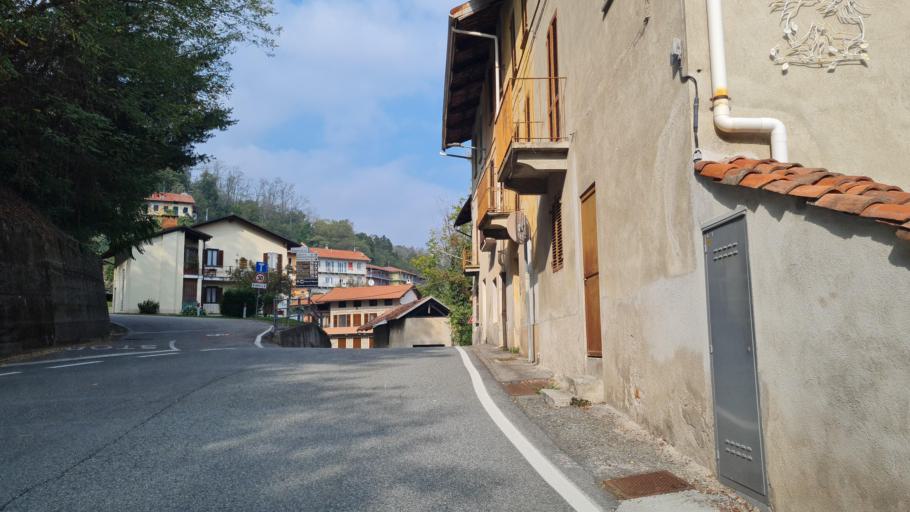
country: IT
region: Piedmont
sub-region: Provincia di Biella
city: Mezzana Mortigliengo
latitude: 45.6235
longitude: 8.1816
